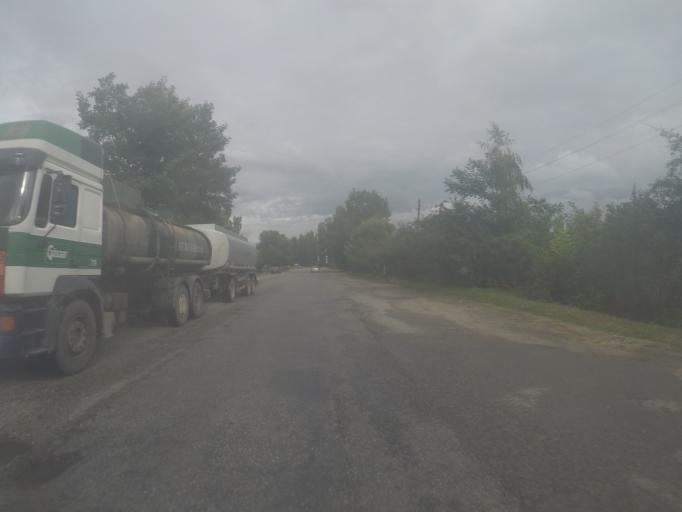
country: KG
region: Ysyk-Koel
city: Tyup
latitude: 42.7421
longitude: 78.0245
